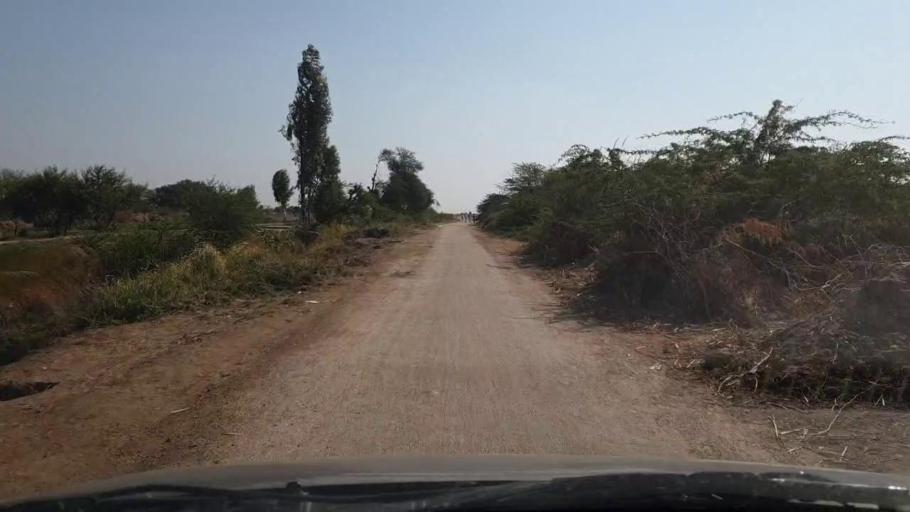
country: PK
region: Sindh
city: Samaro
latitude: 25.2101
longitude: 69.2750
